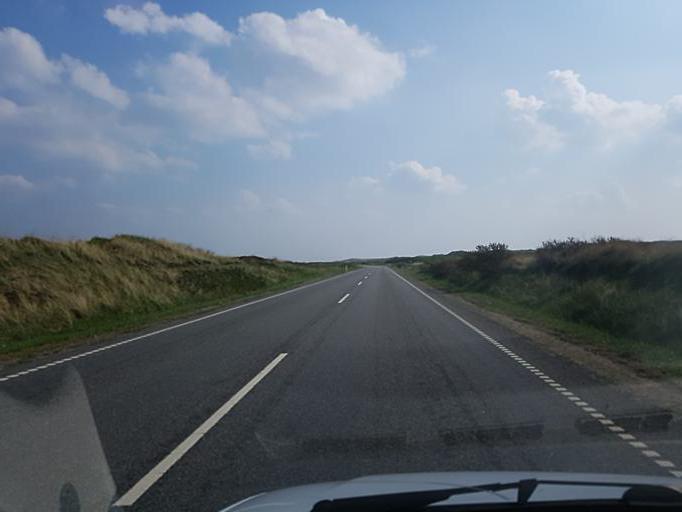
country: DK
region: Central Jutland
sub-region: Ringkobing-Skjern Kommune
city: Hvide Sande
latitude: 55.8297
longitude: 8.1727
